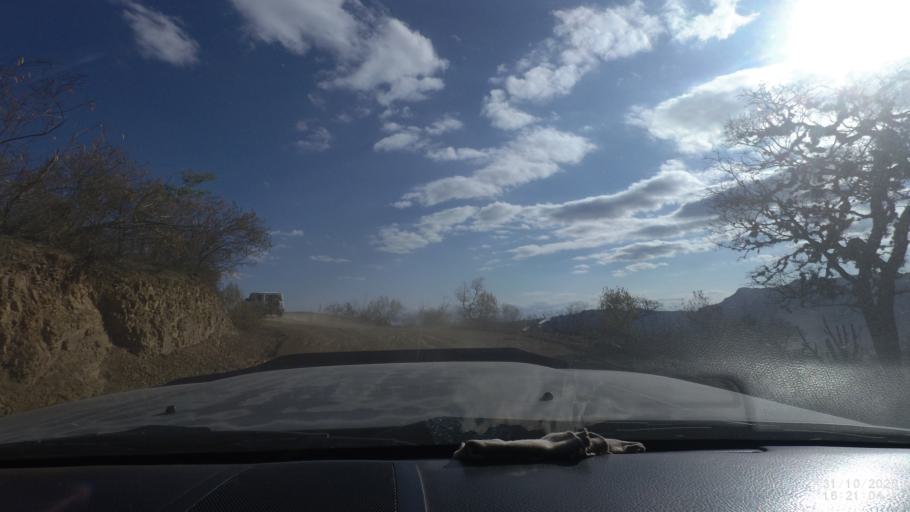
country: BO
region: Chuquisaca
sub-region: Provincia Zudanez
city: Mojocoya
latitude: -18.3977
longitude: -64.5991
